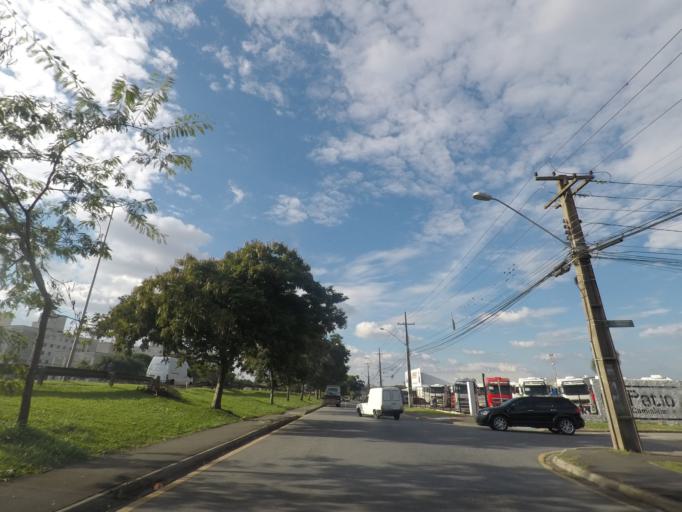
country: BR
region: Parana
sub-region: Sao Jose Dos Pinhais
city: Sao Jose dos Pinhais
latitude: -25.5114
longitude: -49.2878
